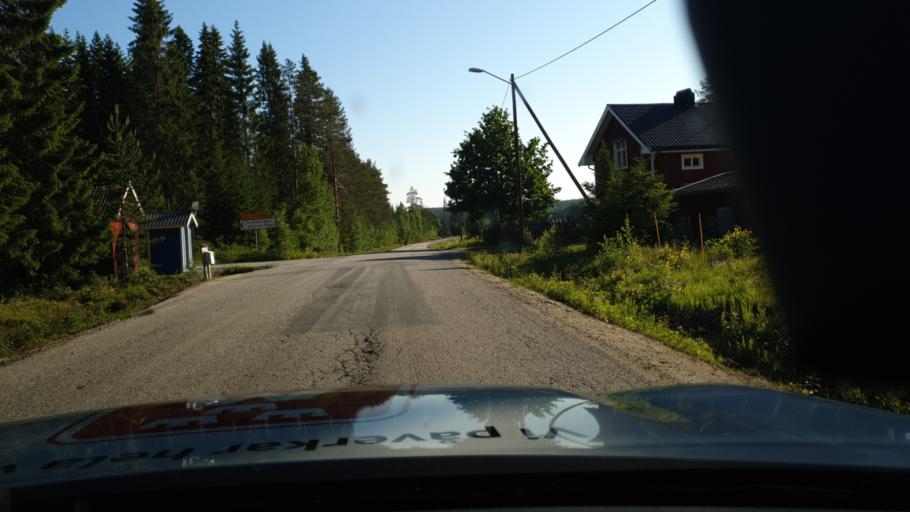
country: SE
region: Vaesterbotten
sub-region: Umea Kommun
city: Roback
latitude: 64.0183
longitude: 20.0820
